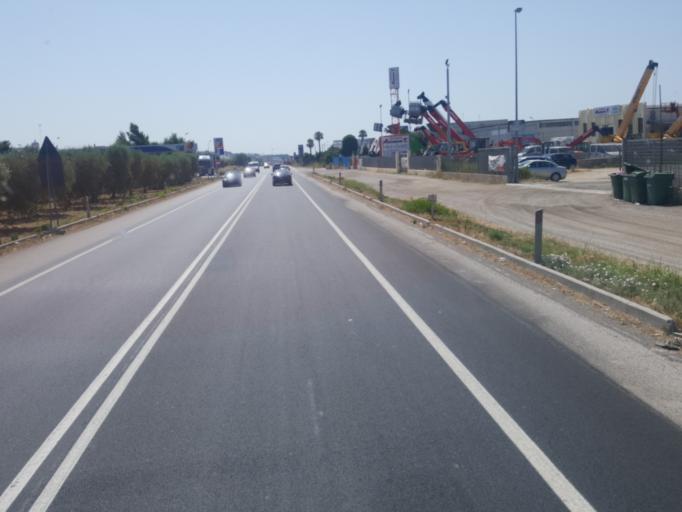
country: IT
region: Apulia
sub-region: Provincia di Taranto
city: Massafra
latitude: 40.5934
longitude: 17.0920
